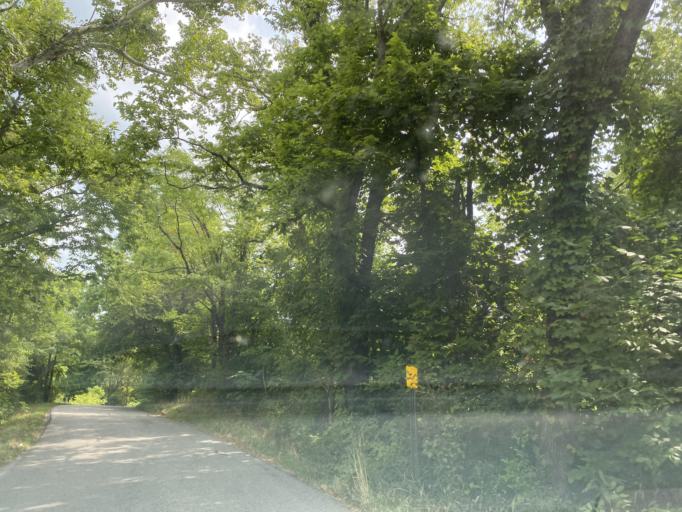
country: US
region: Kentucky
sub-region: Pendleton County
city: Falmouth
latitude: 38.7967
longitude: -84.3347
